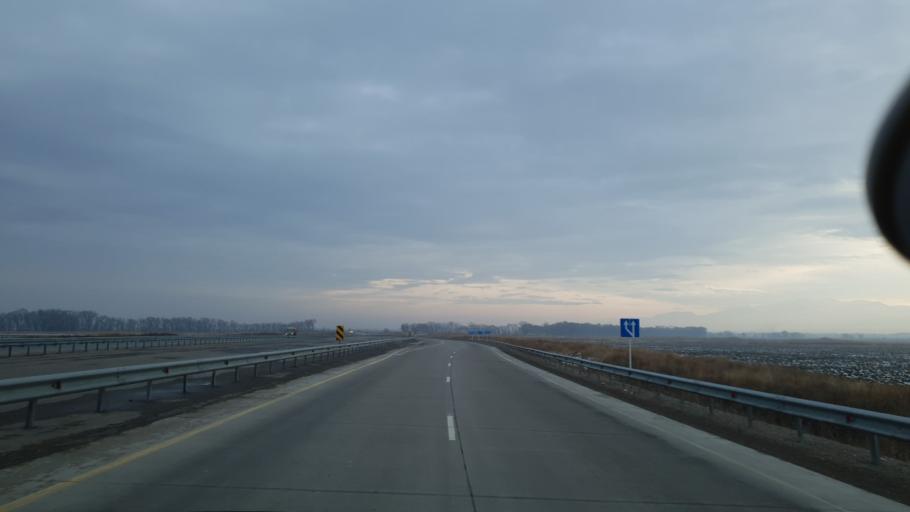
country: KZ
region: Almaty Oblysy
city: Talghar
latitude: 43.4629
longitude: 77.2691
